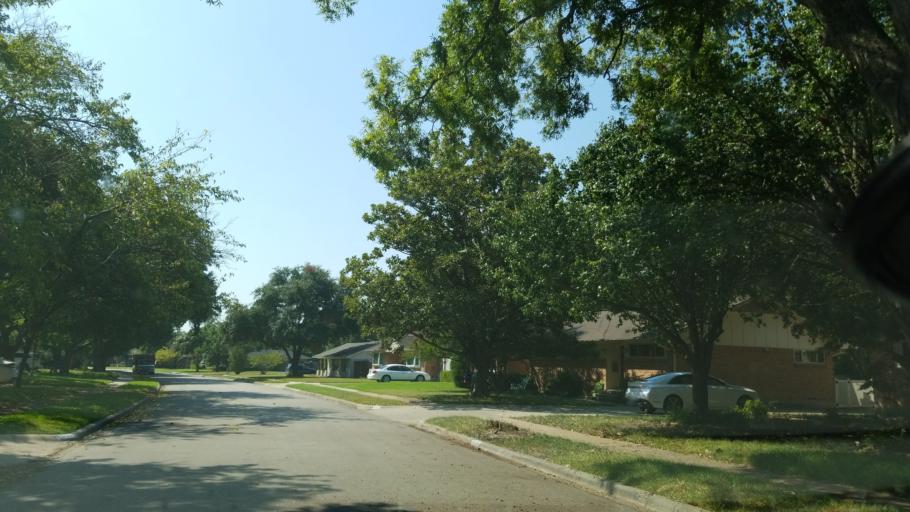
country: US
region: Texas
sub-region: Dallas County
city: Richardson
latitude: 32.8786
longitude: -96.7074
